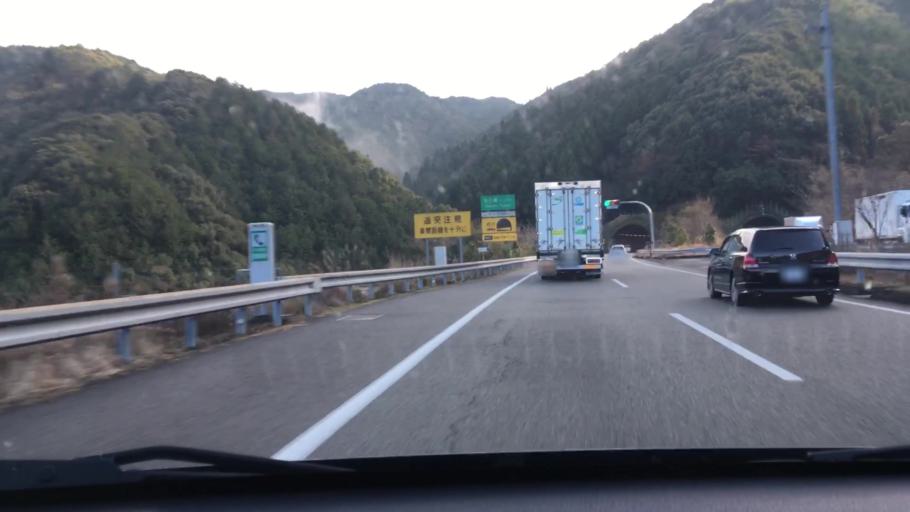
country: JP
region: Kumamoto
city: Hitoyoshi
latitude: 32.1359
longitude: 130.8035
